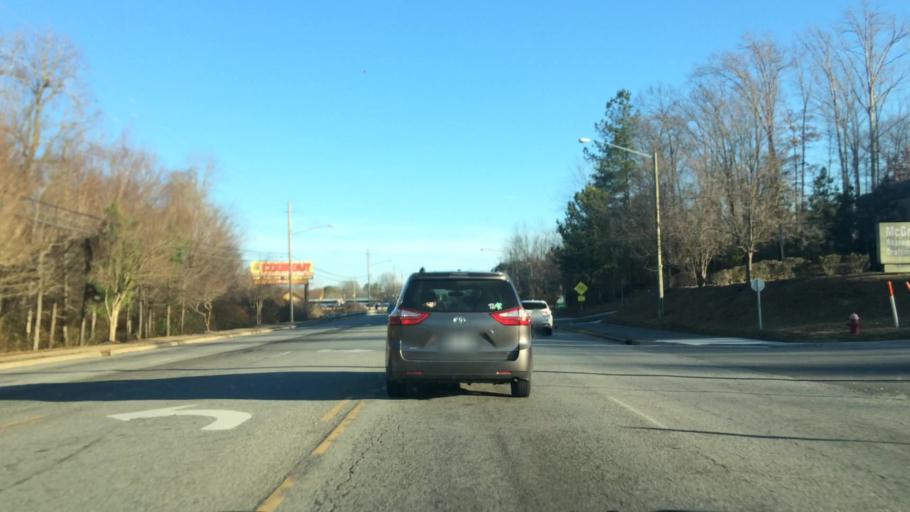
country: US
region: North Carolina
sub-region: Pitt County
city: Greenville
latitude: 35.5918
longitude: -77.3780
